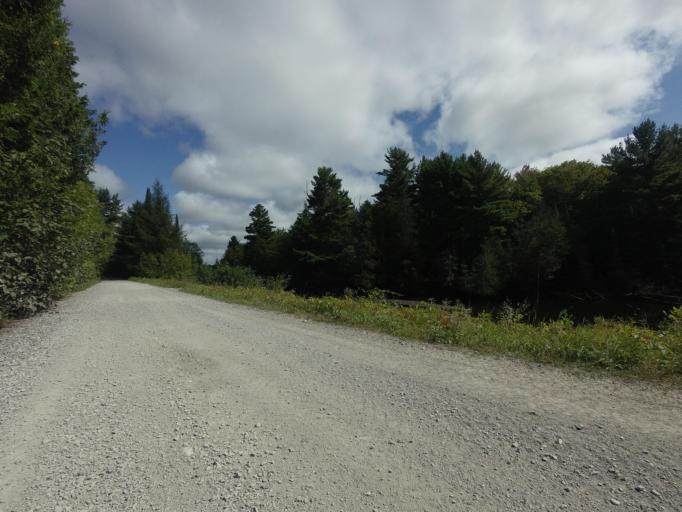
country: CA
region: Ontario
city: Omemee
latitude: 44.7654
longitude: -78.6587
